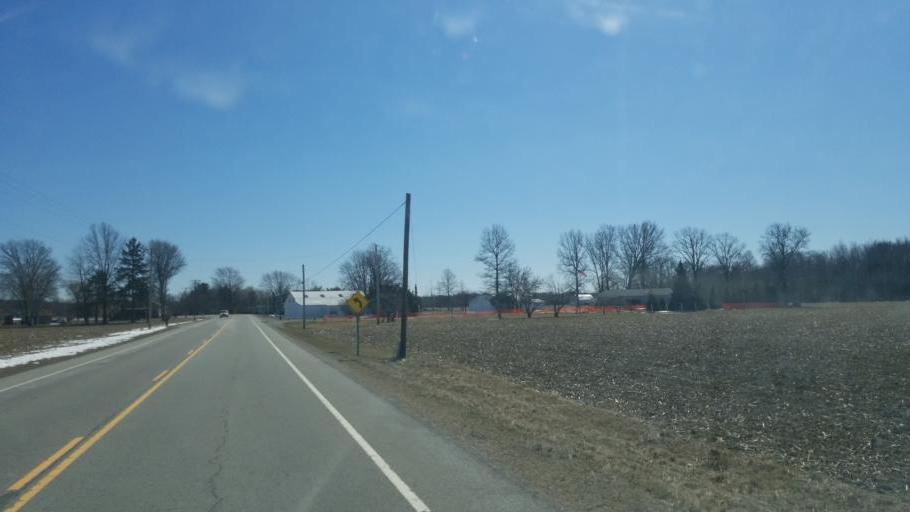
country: US
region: Ohio
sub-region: Crawford County
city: Galion
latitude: 40.8082
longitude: -82.8250
